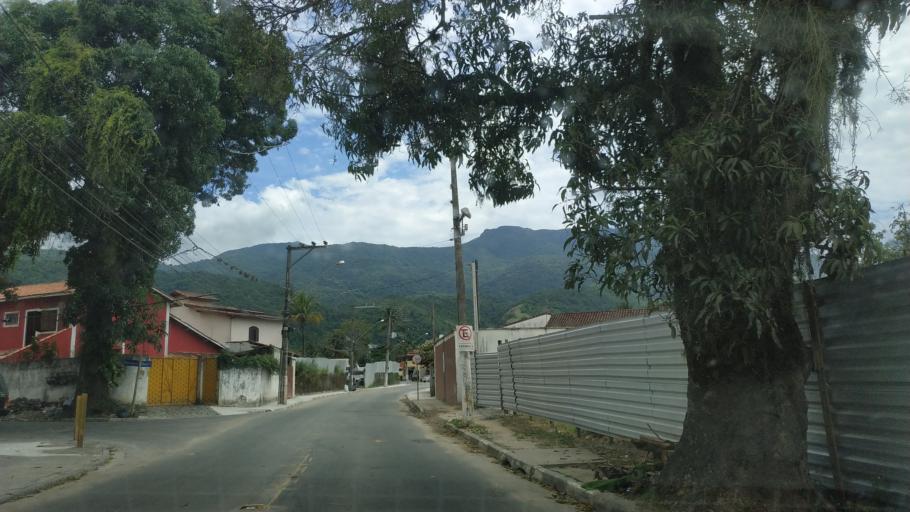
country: BR
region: Sao Paulo
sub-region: Ilhabela
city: Ilhabela
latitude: -23.8204
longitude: -45.3613
